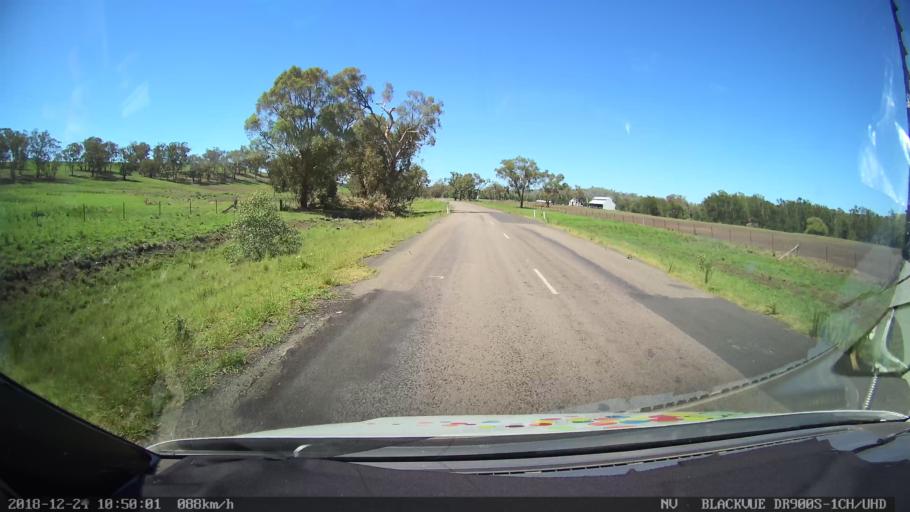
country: AU
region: New South Wales
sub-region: Upper Hunter Shire
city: Merriwa
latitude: -31.9547
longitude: 150.4250
